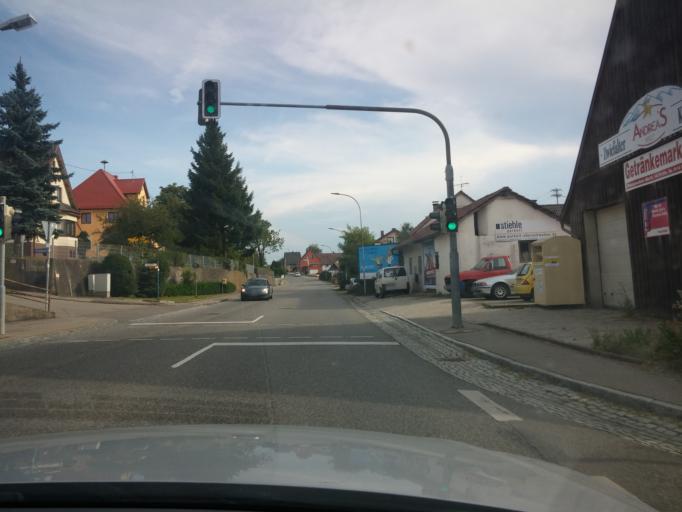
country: DE
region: Baden-Wuerttemberg
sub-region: Tuebingen Region
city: Seekirch
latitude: 48.1272
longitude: 9.6519
